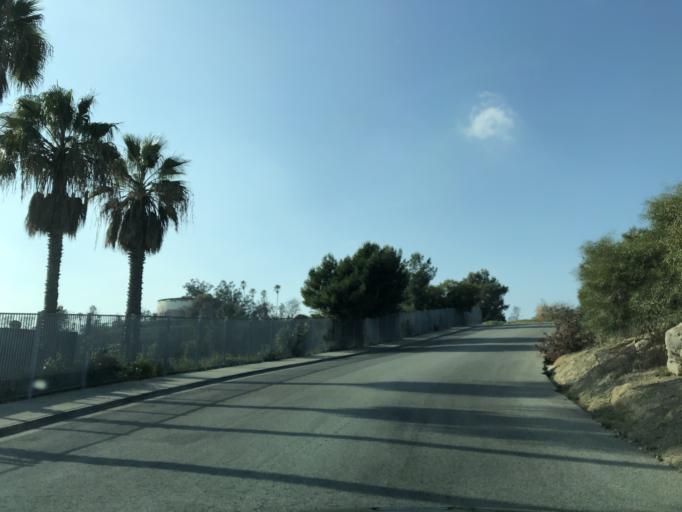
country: US
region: California
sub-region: Los Angeles County
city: Echo Park
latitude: 34.0858
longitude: -118.2378
